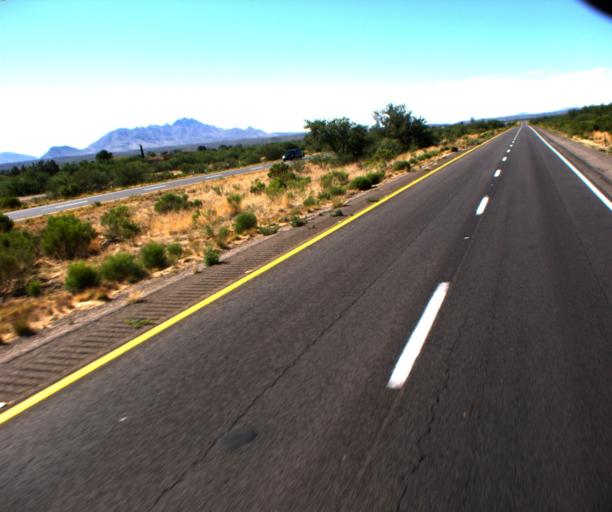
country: US
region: Arizona
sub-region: Santa Cruz County
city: Tubac
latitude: 31.6331
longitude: -111.0563
